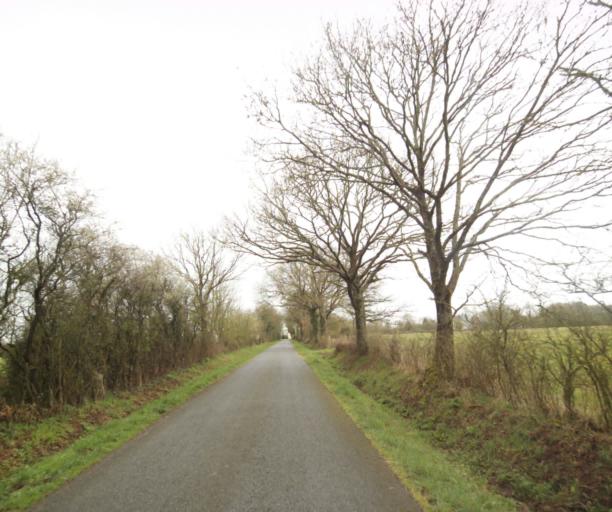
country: FR
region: Pays de la Loire
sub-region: Departement de la Loire-Atlantique
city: Bouvron
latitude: 47.4414
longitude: -1.8511
